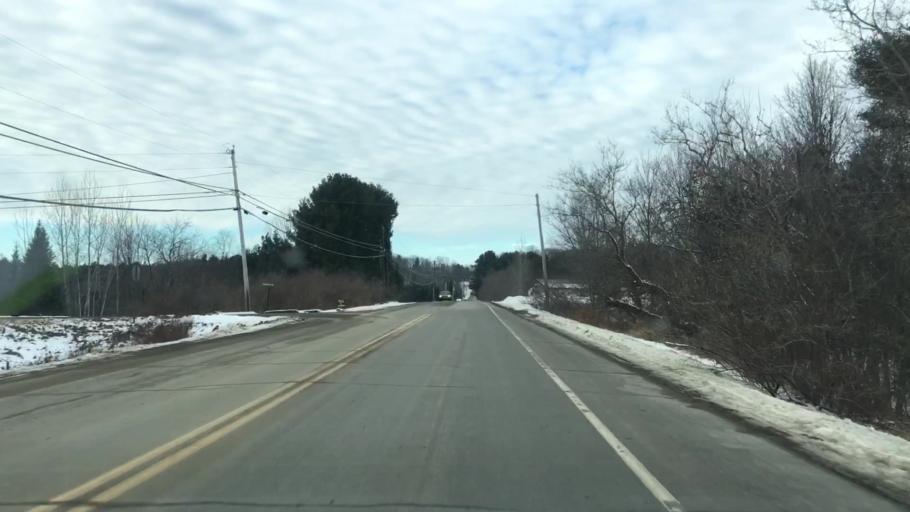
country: US
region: Maine
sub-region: Lincoln County
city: Whitefield
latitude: 44.2249
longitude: -69.6059
